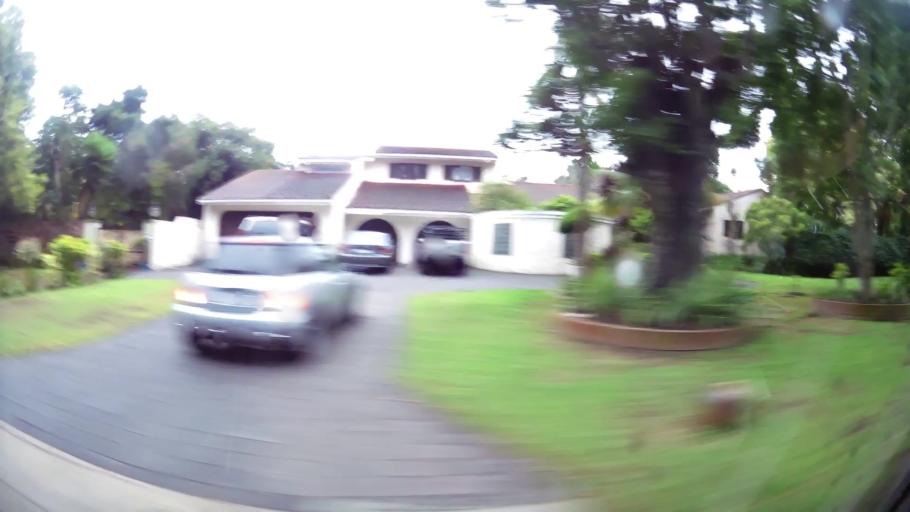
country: ZA
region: Eastern Cape
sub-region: Nelson Mandela Bay Metropolitan Municipality
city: Port Elizabeth
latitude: -33.9768
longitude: 25.5766
